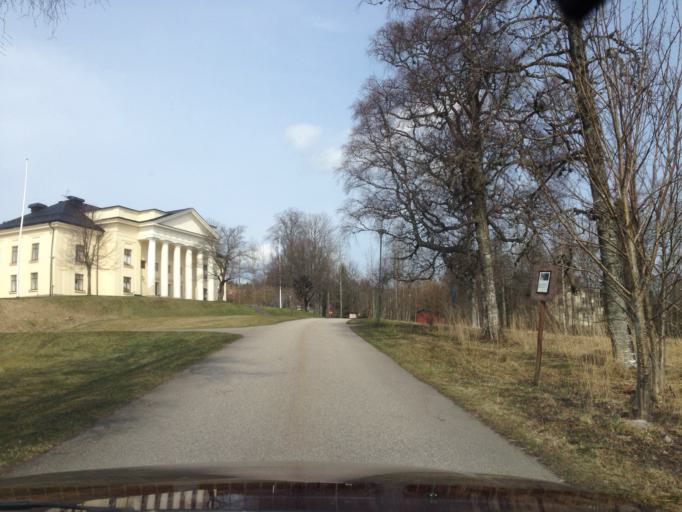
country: SE
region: Dalarna
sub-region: Ludvika Kommun
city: Grangesberg
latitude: 60.0779
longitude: 14.9862
